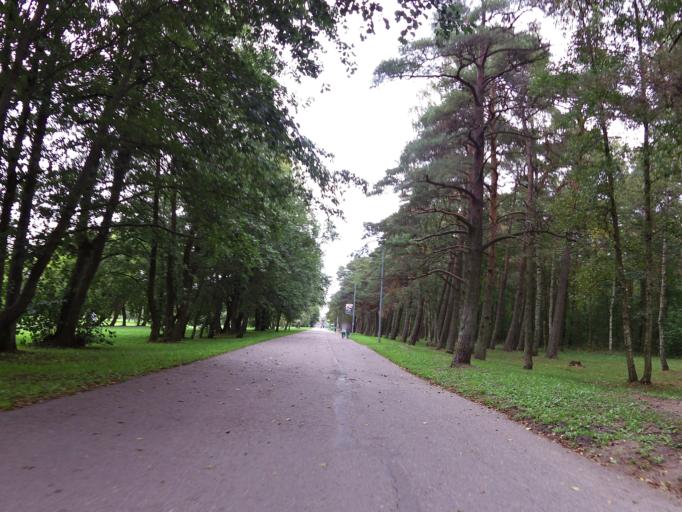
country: EE
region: Harju
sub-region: Tallinna linn
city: Tallinn
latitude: 59.4363
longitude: 24.6835
